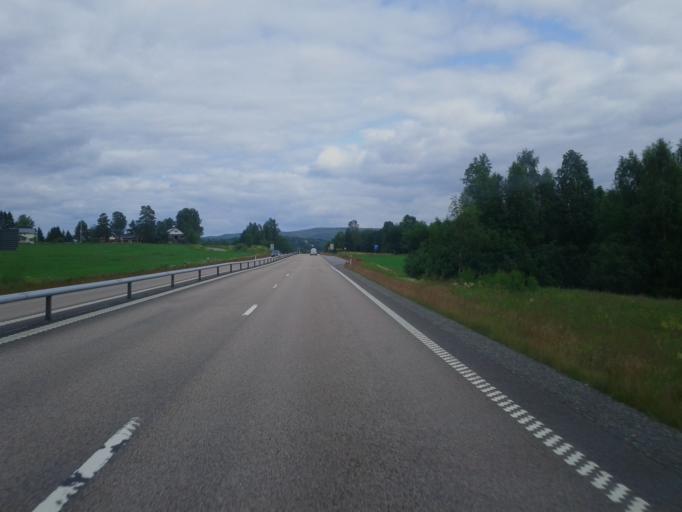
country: SE
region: Vaesternorrland
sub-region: OErnskoeldsviks Kommun
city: Bjasta
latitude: 63.2674
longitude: 18.5306
